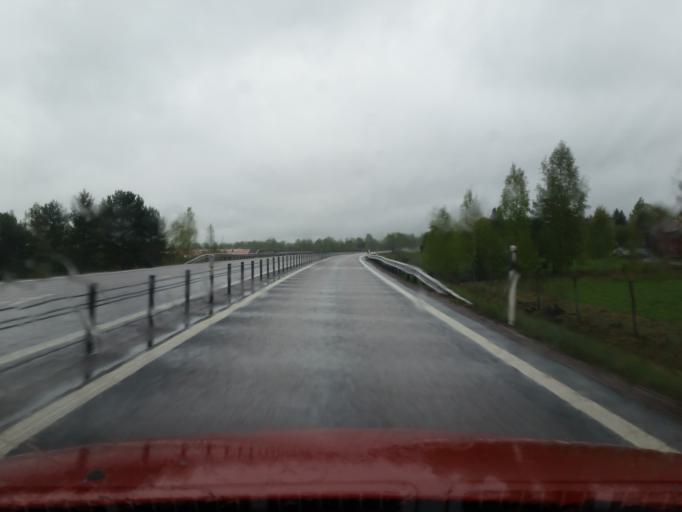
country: SE
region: Dalarna
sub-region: Borlange Kommun
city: Ornas
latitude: 60.4087
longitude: 15.6011
